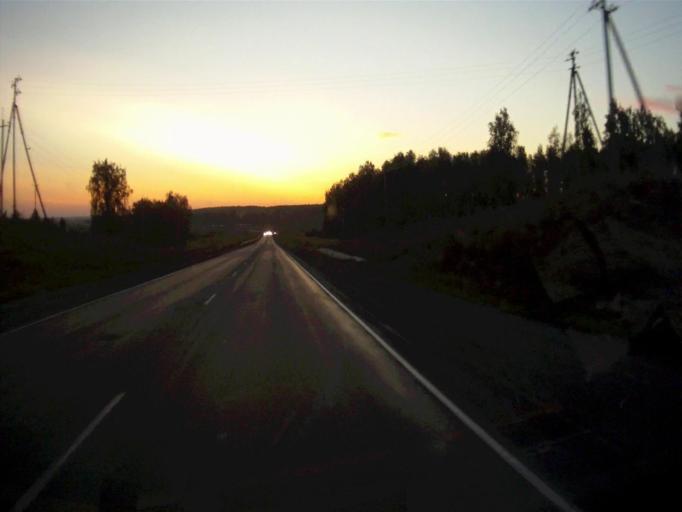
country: RU
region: Chelyabinsk
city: Poletayevo
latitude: 55.2230
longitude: 61.0096
